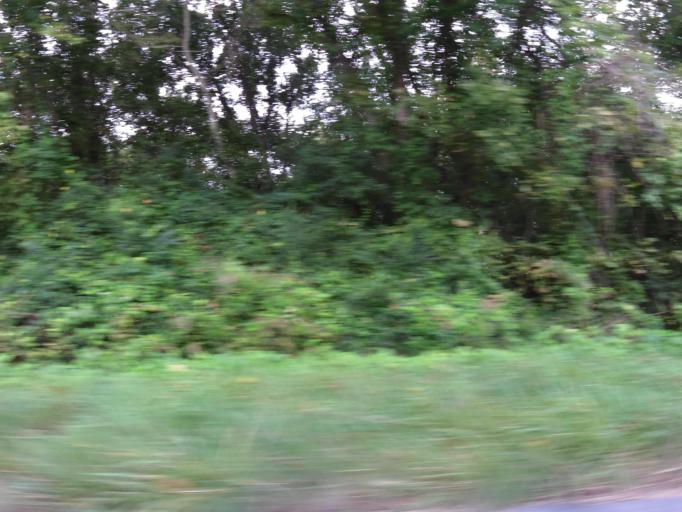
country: US
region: Tennessee
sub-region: Campbell County
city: Jellico
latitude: 36.5996
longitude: -84.1257
